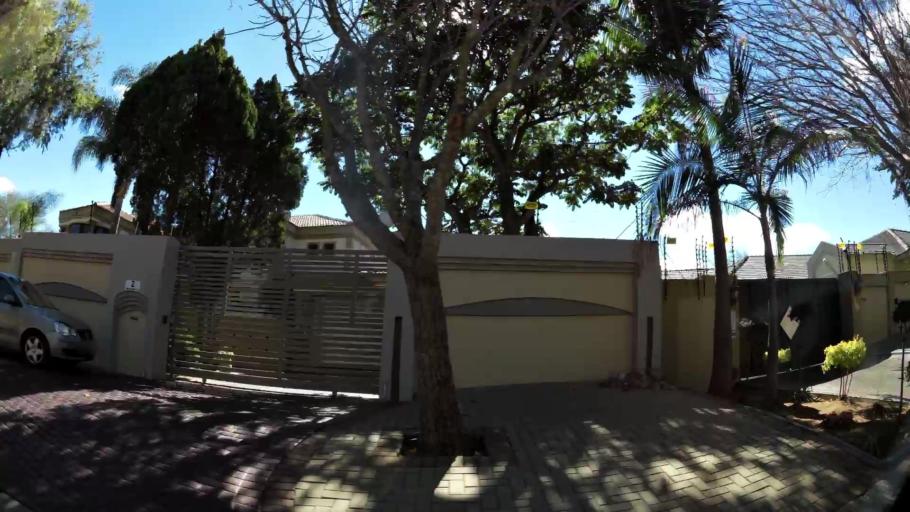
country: ZA
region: Limpopo
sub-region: Capricorn District Municipality
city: Polokwane
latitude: -23.9072
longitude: 29.4786
